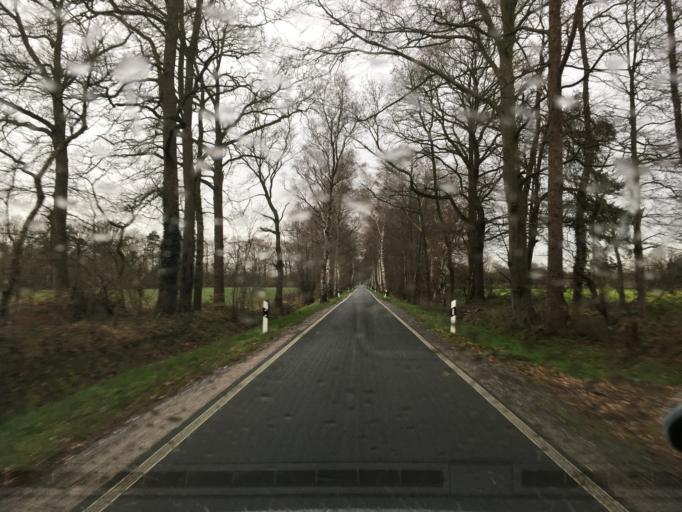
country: DE
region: North Rhine-Westphalia
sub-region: Regierungsbezirk Munster
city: Heek
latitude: 52.1379
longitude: 7.1444
